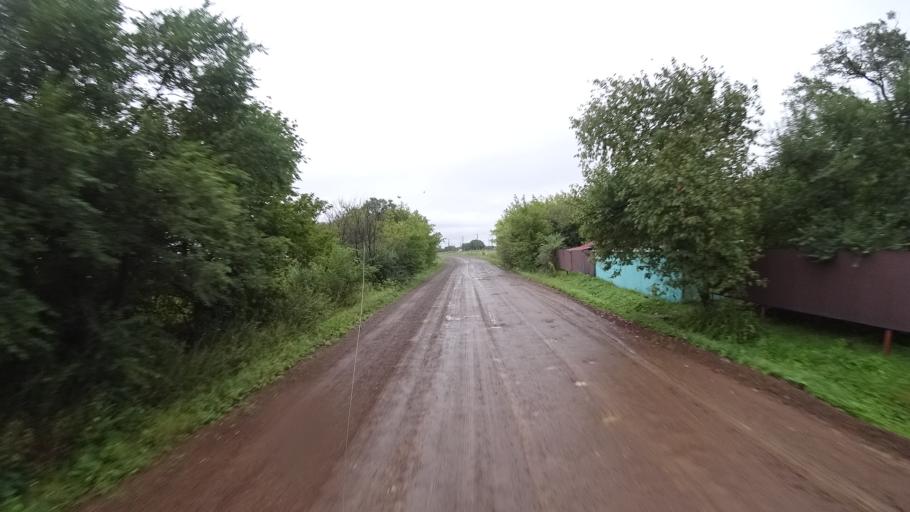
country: RU
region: Primorskiy
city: Monastyrishche
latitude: 44.2756
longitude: 132.4587
